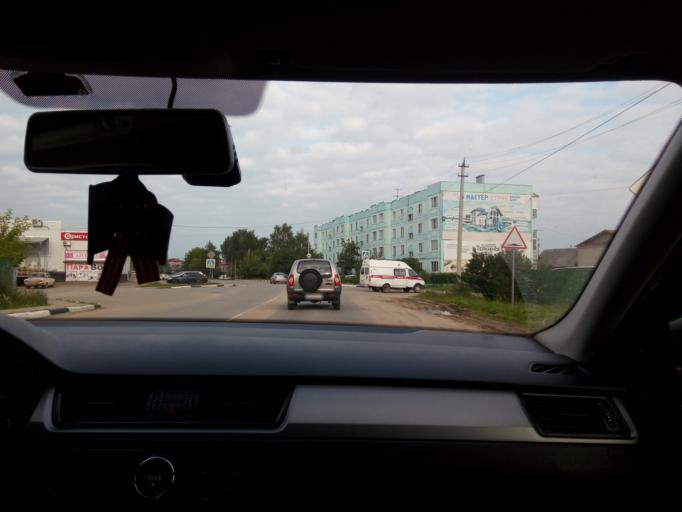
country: RU
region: Nizjnij Novgorod
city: Voskresenskoye
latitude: 56.8381
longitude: 45.4273
